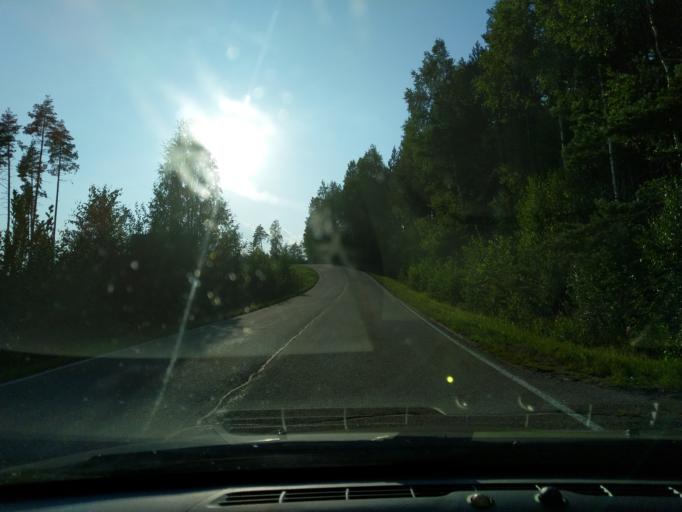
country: FI
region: Uusimaa
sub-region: Helsinki
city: Vihti
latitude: 60.5329
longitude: 24.3468
